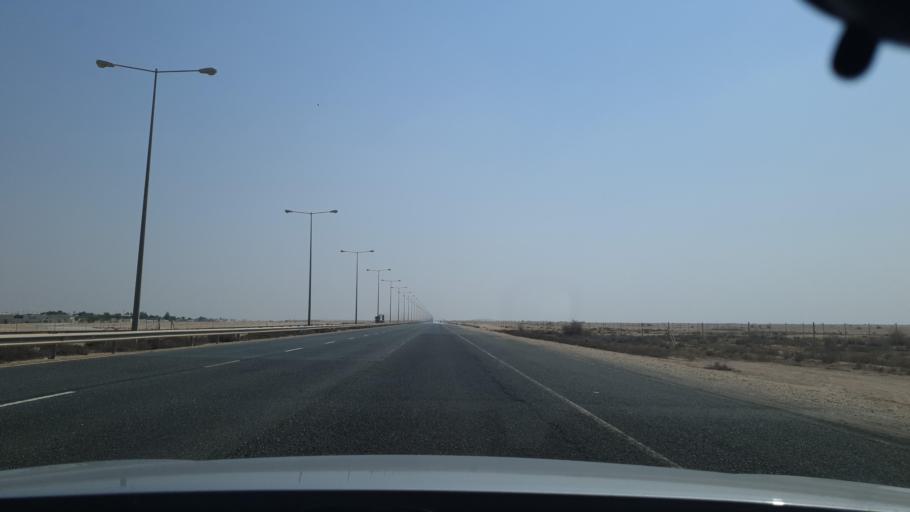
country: QA
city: Al Ghuwayriyah
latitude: 25.8155
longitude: 51.3703
